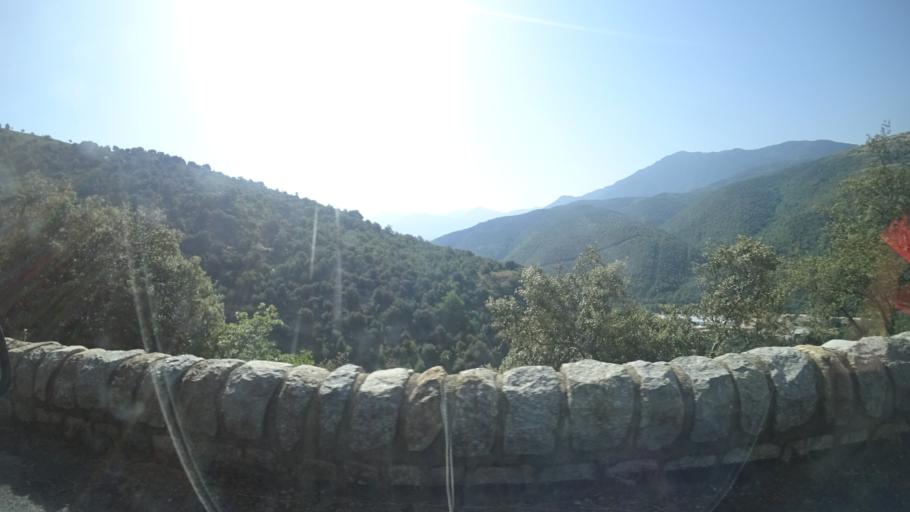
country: FR
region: Languedoc-Roussillon
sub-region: Departement des Pyrenees-Orientales
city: Vernet-les-Bains
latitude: 42.5649
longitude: 2.2911
